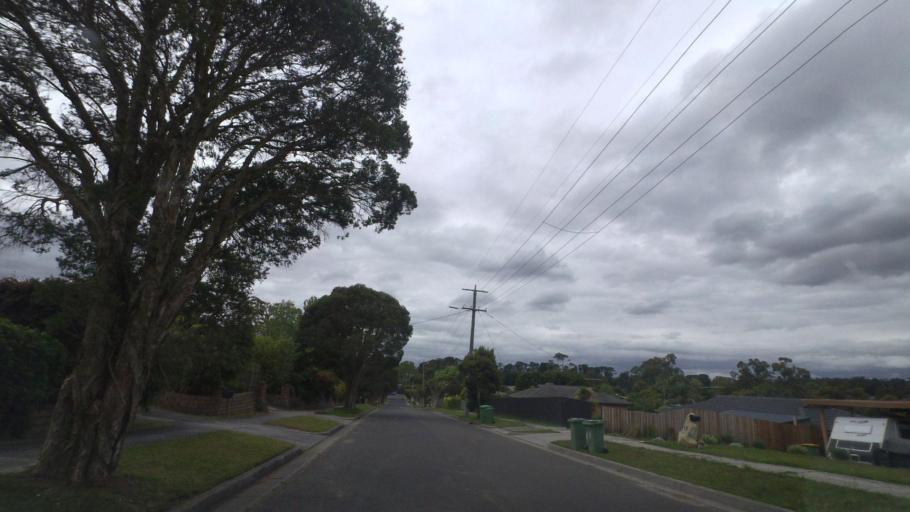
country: AU
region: Victoria
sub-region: Yarra Ranges
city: Mount Evelyn
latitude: -37.7890
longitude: 145.3710
